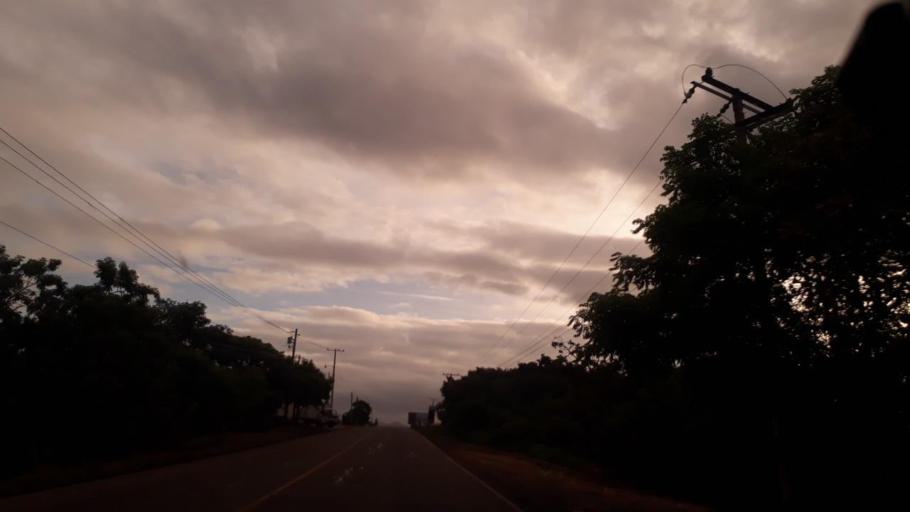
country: GT
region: Jutiapa
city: El Progreso
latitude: 14.3324
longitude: -89.8574
